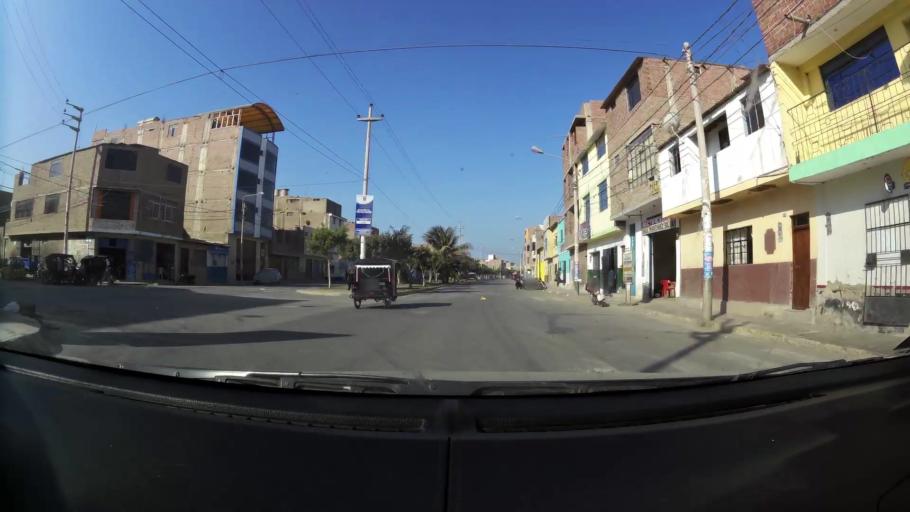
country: PE
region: Lambayeque
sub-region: Provincia de Chiclayo
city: Chiclayo
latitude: -6.7635
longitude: -79.8491
